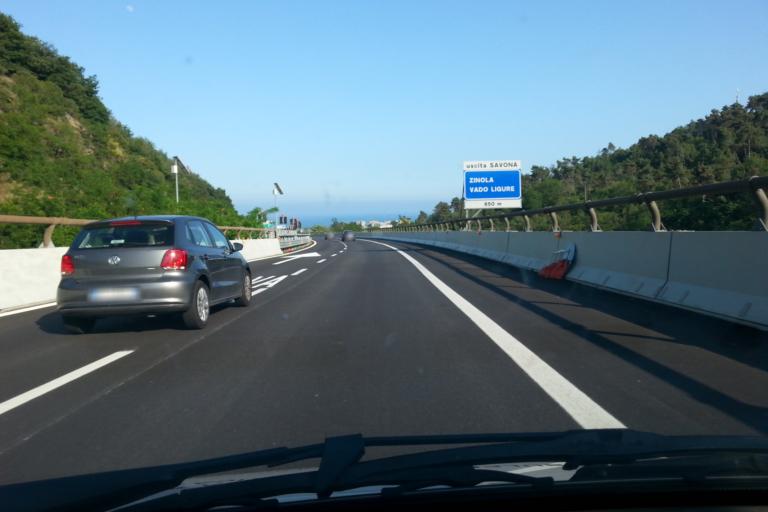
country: IT
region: Liguria
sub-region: Provincia di Savona
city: Valleggia
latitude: 44.2933
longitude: 8.4342
